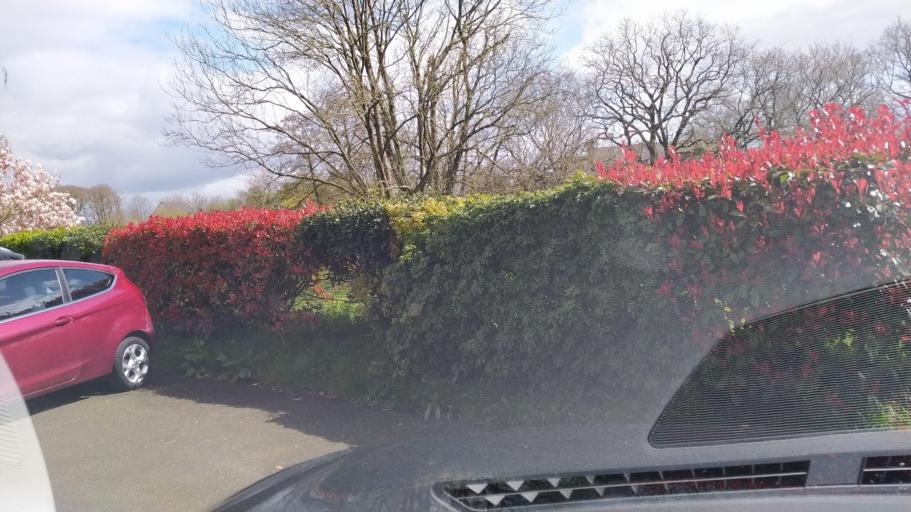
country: FR
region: Brittany
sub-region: Departement du Finistere
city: Bodilis
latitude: 48.5296
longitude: -4.1150
